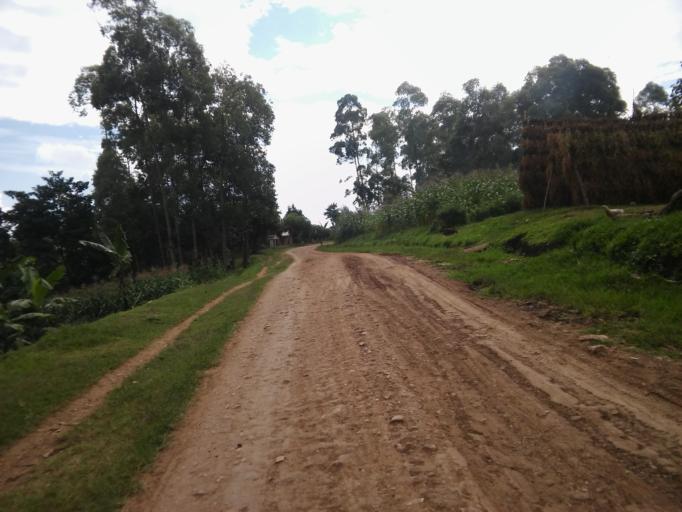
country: UG
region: Eastern Region
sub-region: Manafwa District
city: Manafwa
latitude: 0.8956
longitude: 34.3591
